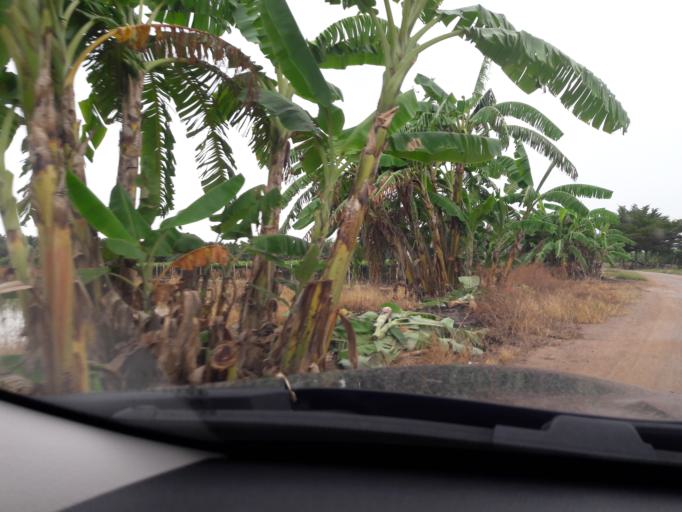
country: TH
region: Ratchaburi
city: Bang Phae
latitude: 13.6191
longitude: 99.9620
